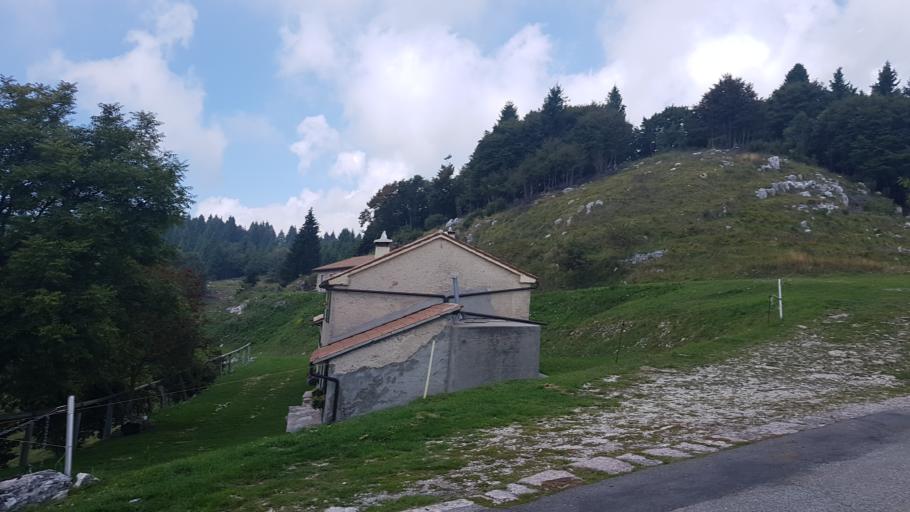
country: IT
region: Veneto
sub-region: Provincia di Treviso
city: Borso del Grappa
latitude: 45.8488
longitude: 11.7939
